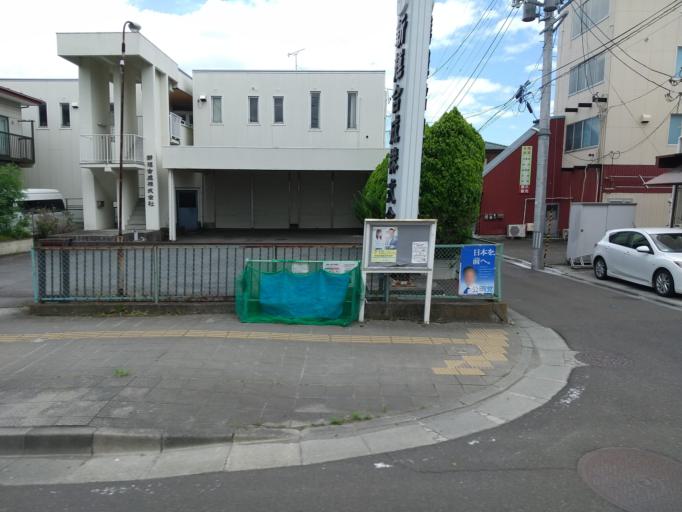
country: JP
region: Miyagi
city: Sendai-shi
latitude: 38.2649
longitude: 140.9302
